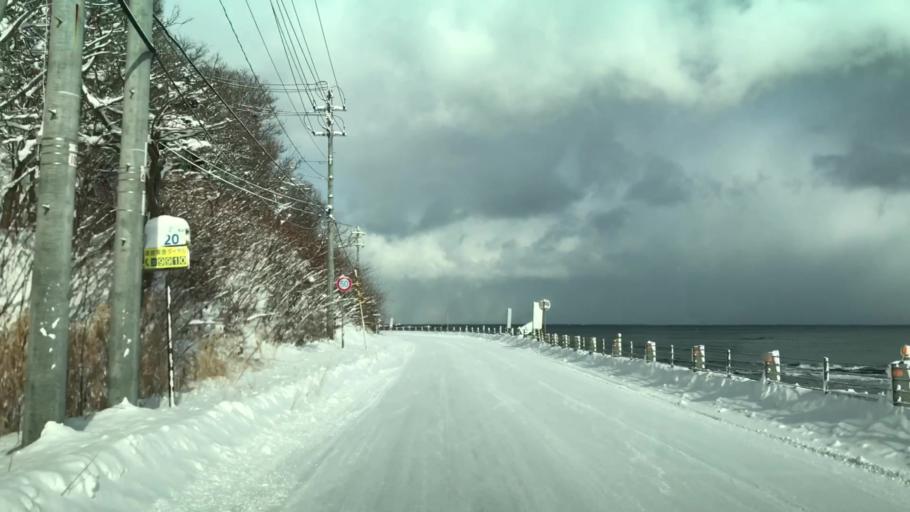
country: JP
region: Hokkaido
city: Yoichi
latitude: 43.2873
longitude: 140.6337
